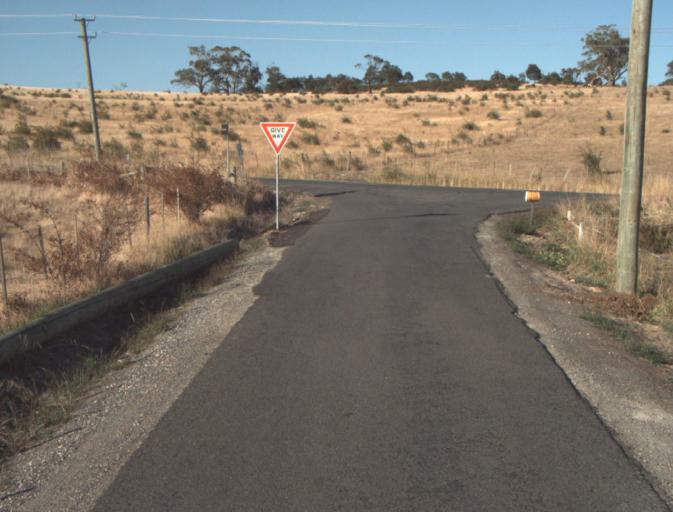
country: AU
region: Tasmania
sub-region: Launceston
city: Newstead
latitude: -41.4378
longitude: 147.2100
